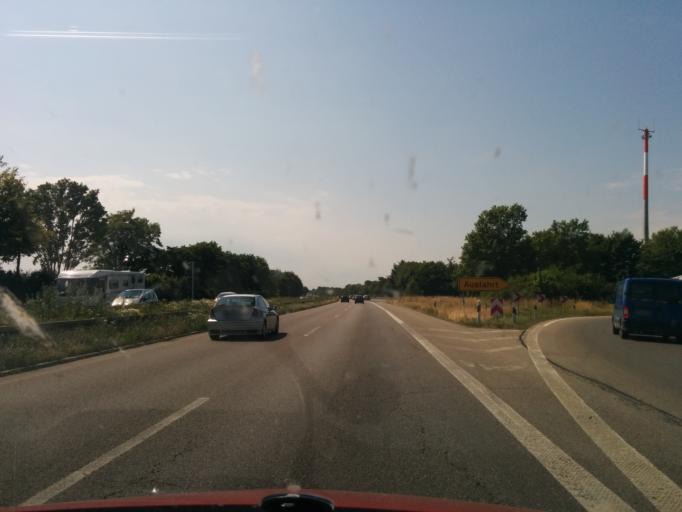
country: DE
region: Bavaria
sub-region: Swabia
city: Konigsbrunn
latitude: 48.2604
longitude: 10.8661
